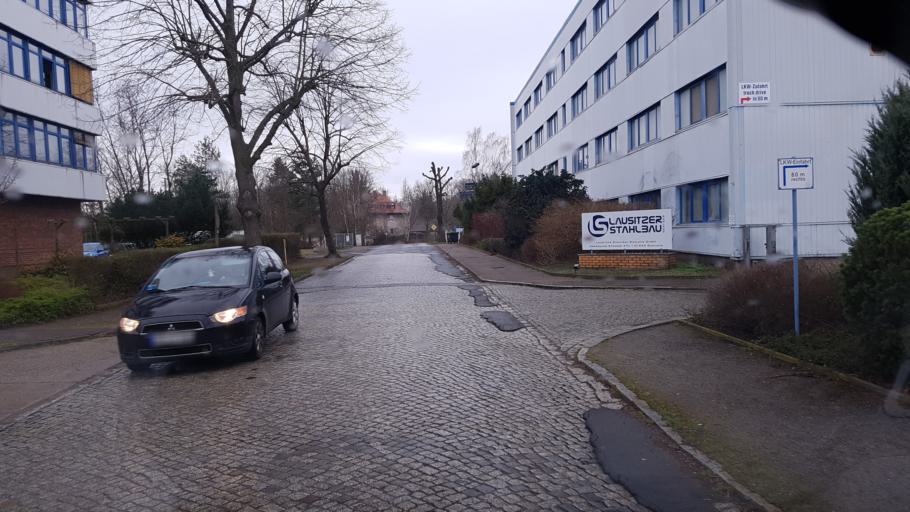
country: DE
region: Brandenburg
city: Ruhland
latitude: 51.4520
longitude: 13.8630
